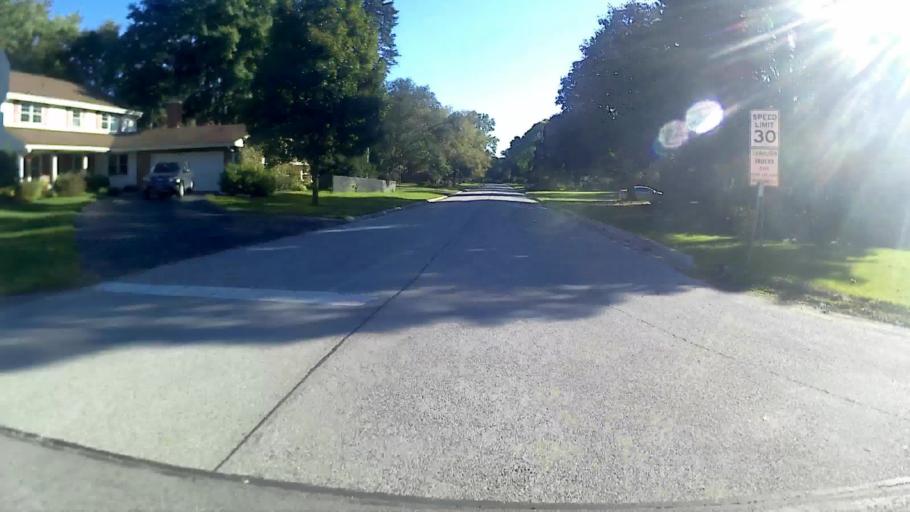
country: US
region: Illinois
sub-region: DuPage County
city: Wheaton
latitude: 41.8498
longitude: -88.1034
